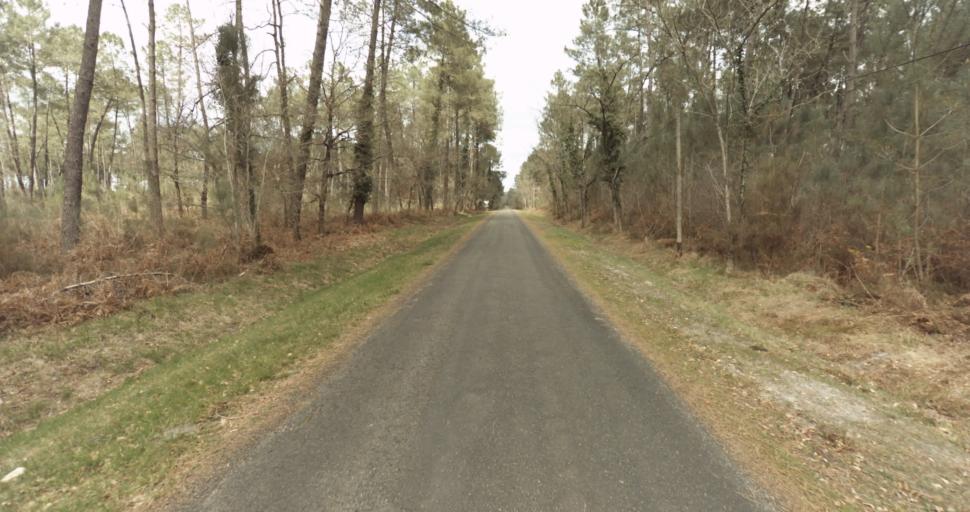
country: FR
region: Aquitaine
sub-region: Departement des Landes
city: Roquefort
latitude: 44.0530
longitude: -0.3780
